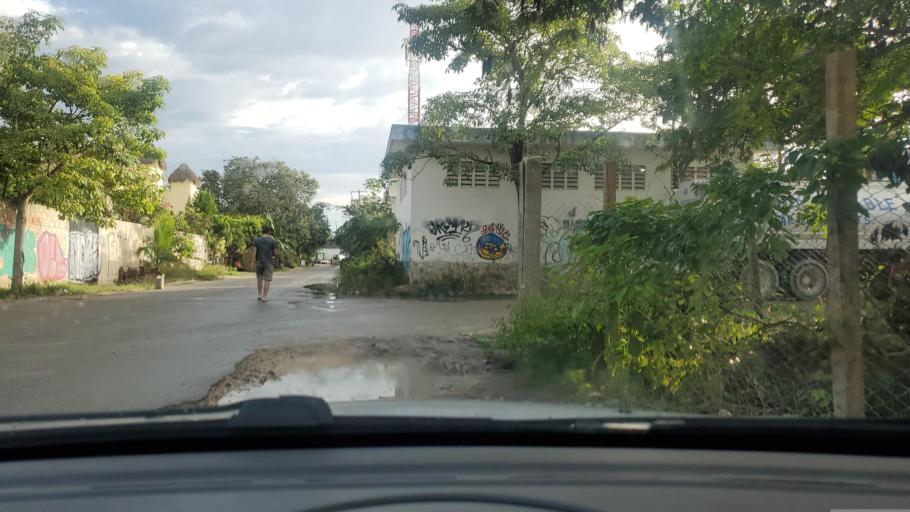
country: MX
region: Quintana Roo
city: Tulum
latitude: 20.2144
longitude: -87.4552
